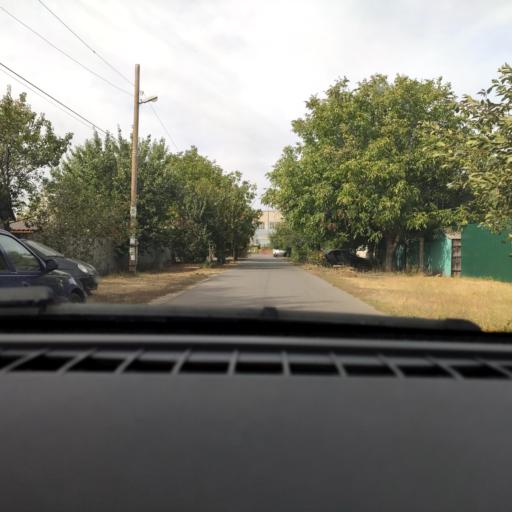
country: RU
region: Voronezj
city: Voronezh
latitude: 51.6697
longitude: 39.2655
